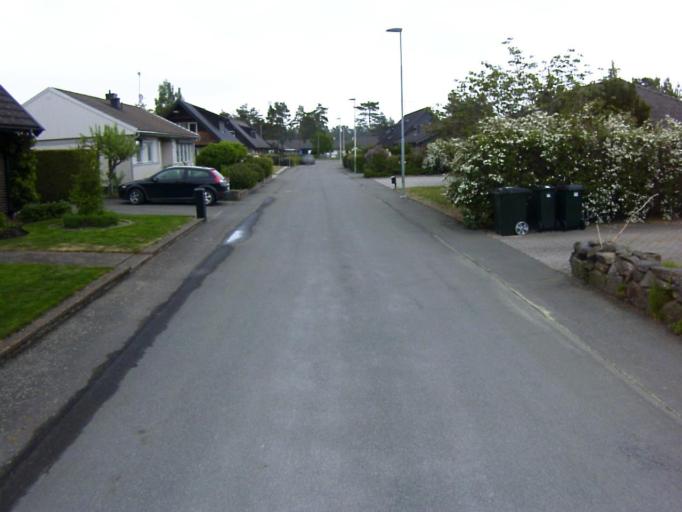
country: SE
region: Skane
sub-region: Kristianstads Kommun
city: Ahus
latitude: 55.9376
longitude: 14.2821
